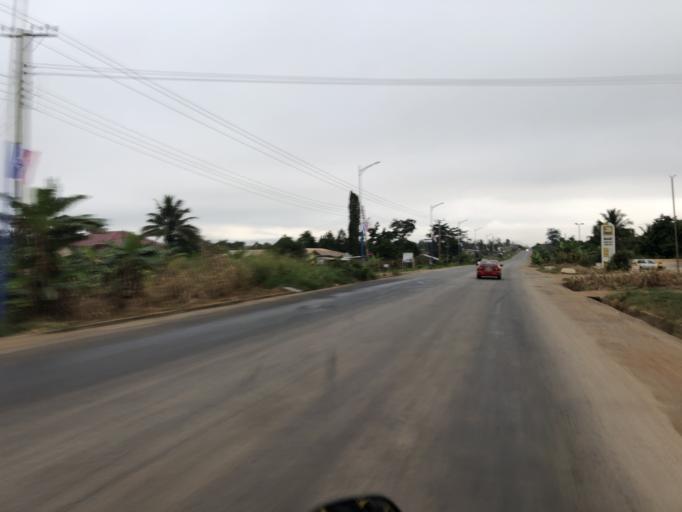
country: GH
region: Eastern
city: Koforidua
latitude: 6.1837
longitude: -0.3505
